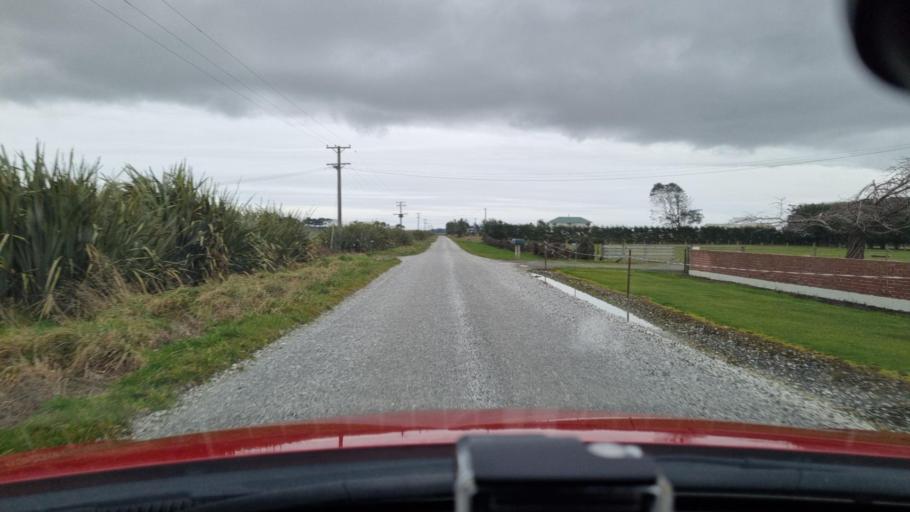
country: NZ
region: Southland
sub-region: Invercargill City
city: Invercargill
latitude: -46.3806
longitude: 168.2866
